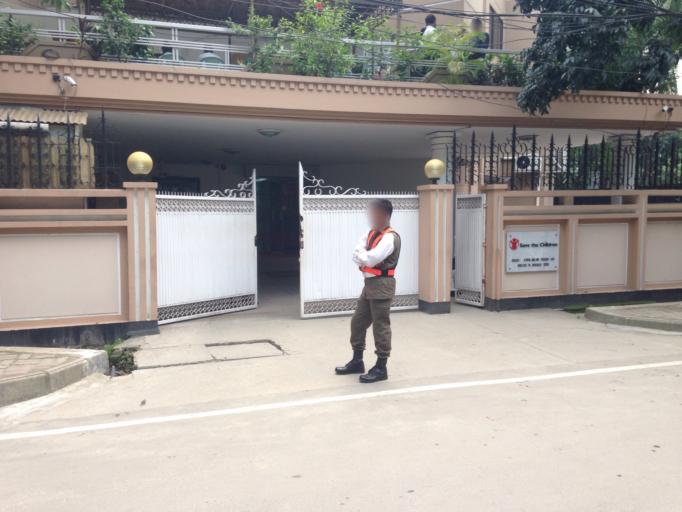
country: BD
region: Dhaka
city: Paltan
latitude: 23.7917
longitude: 90.4115
